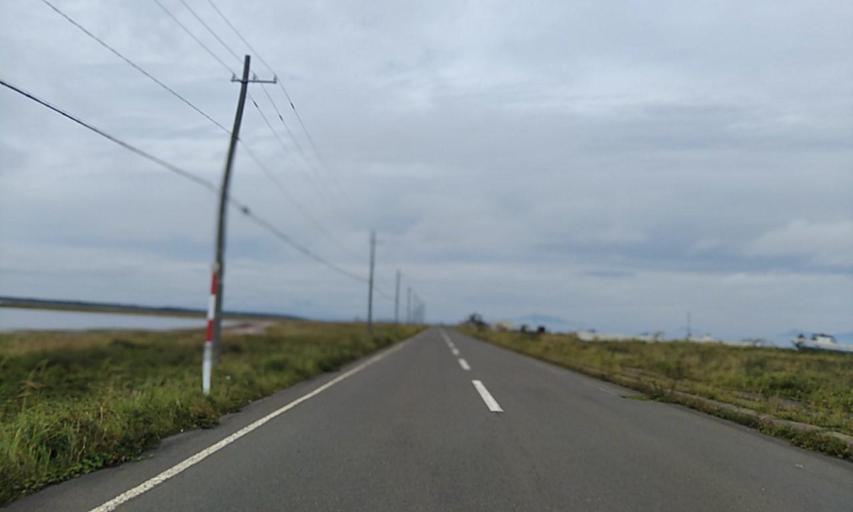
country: JP
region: Hokkaido
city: Shibetsu
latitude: 43.5944
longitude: 145.3279
